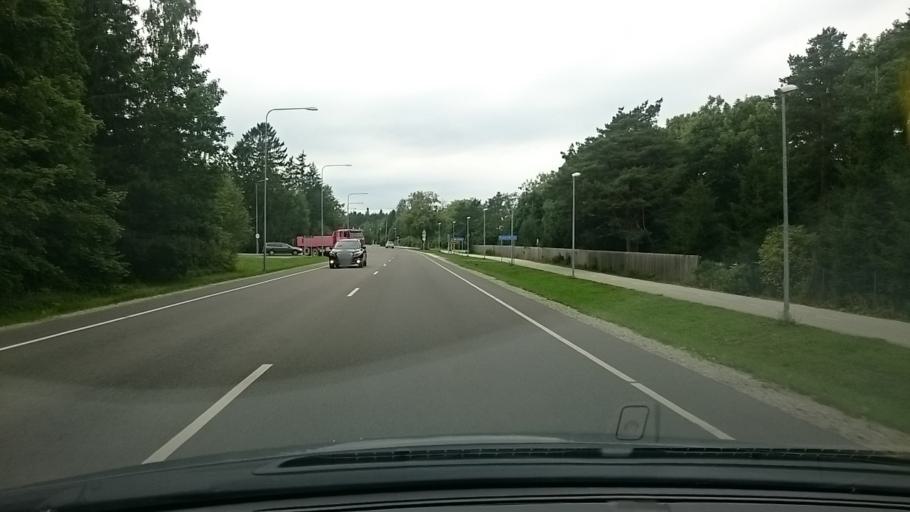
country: EE
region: Harju
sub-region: Harku vald
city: Tabasalu
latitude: 59.4358
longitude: 24.5187
